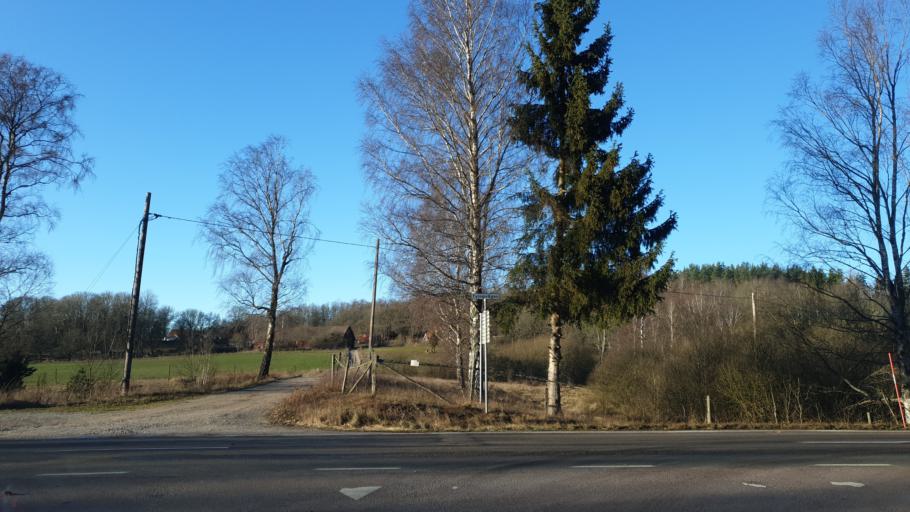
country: SE
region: Blekinge
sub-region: Karlskrona Kommun
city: Nattraby
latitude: 56.2622
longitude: 15.4275
